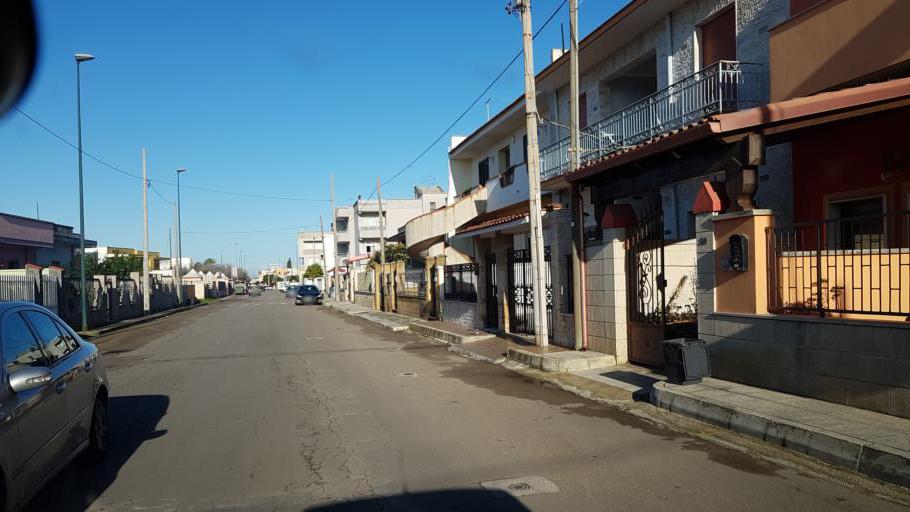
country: IT
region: Apulia
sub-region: Provincia di Brindisi
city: Torchiarolo
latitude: 40.4830
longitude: 18.0496
